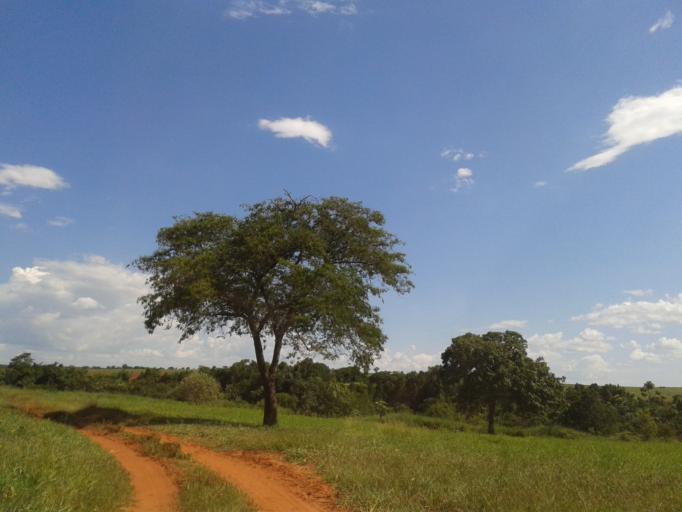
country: BR
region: Minas Gerais
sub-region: Santa Vitoria
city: Santa Vitoria
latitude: -19.1198
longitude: -50.5016
